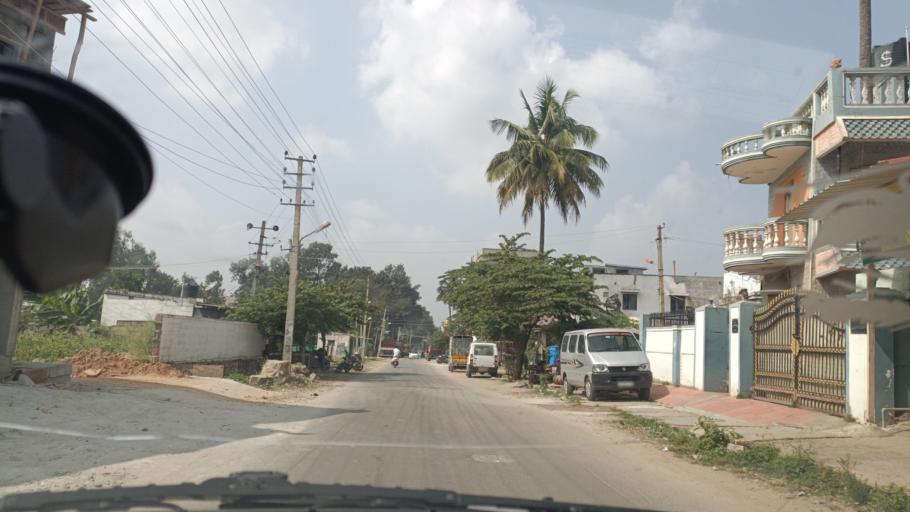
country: IN
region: Karnataka
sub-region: Bangalore Urban
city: Yelahanka
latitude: 13.1565
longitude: 77.6203
